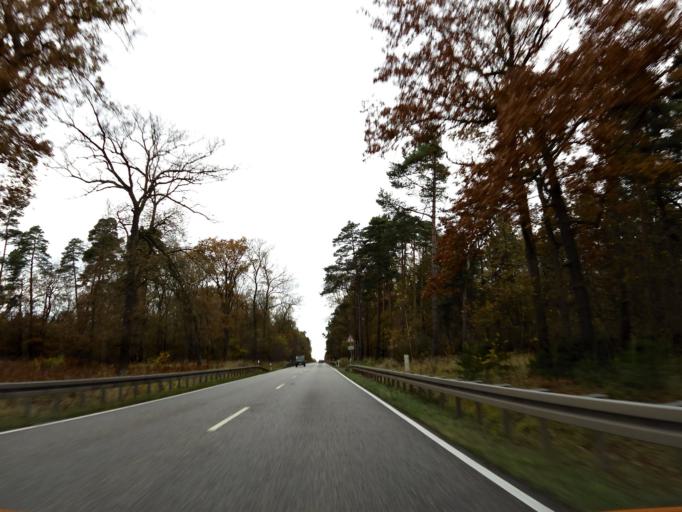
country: DE
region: Saxony-Anhalt
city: Colbitz
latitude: 52.3413
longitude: 11.5797
